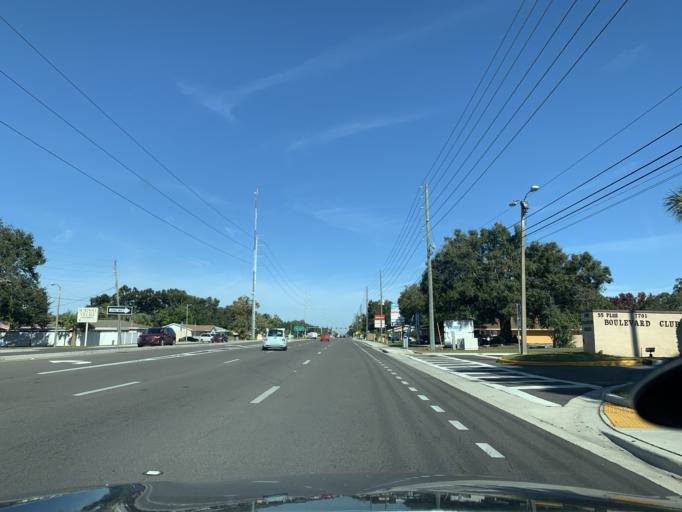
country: US
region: Florida
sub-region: Pinellas County
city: Seminole
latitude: 27.8419
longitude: -82.7622
